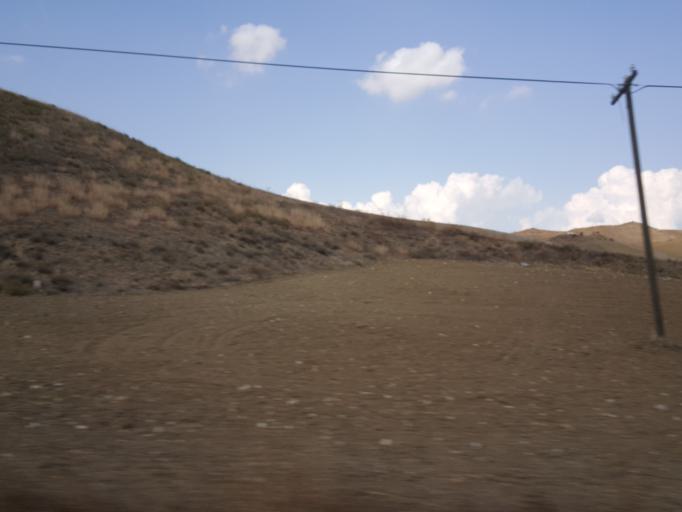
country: TR
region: Corum
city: Bogazkale
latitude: 40.1405
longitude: 34.5684
